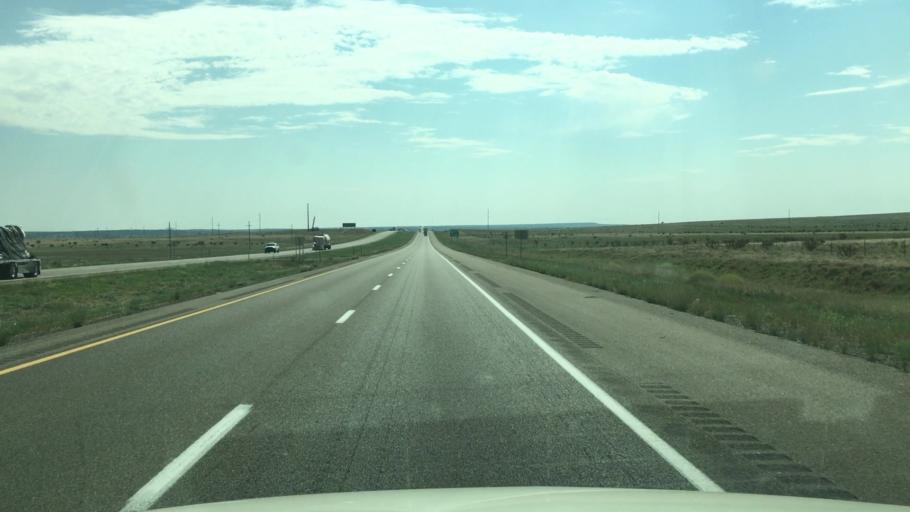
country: US
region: New Mexico
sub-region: Guadalupe County
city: Santa Rosa
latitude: 34.9785
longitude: -105.0336
